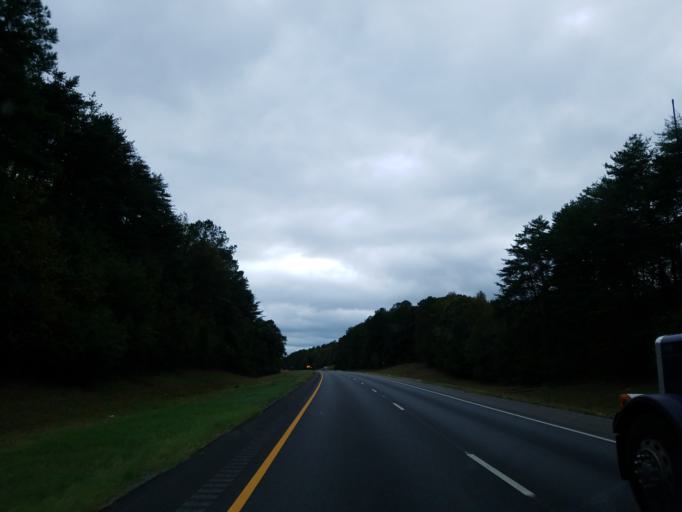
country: US
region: Alabama
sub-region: Hale County
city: Moundville
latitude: 33.0482
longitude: -87.7249
